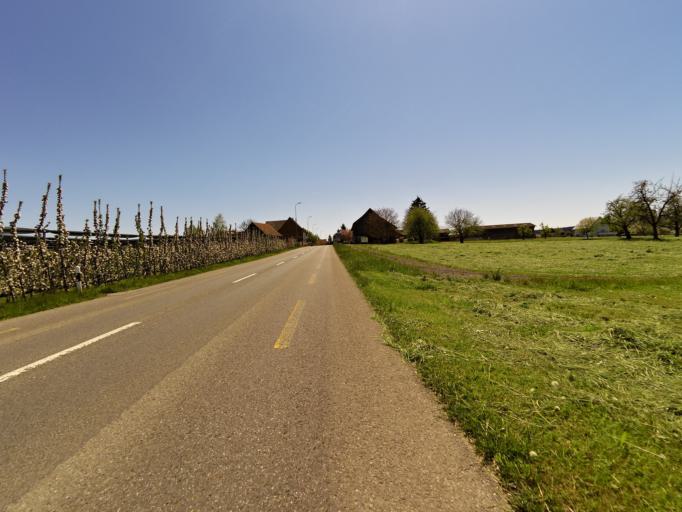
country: CH
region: Thurgau
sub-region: Weinfelden District
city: Berg
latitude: 47.6037
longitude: 9.1704
